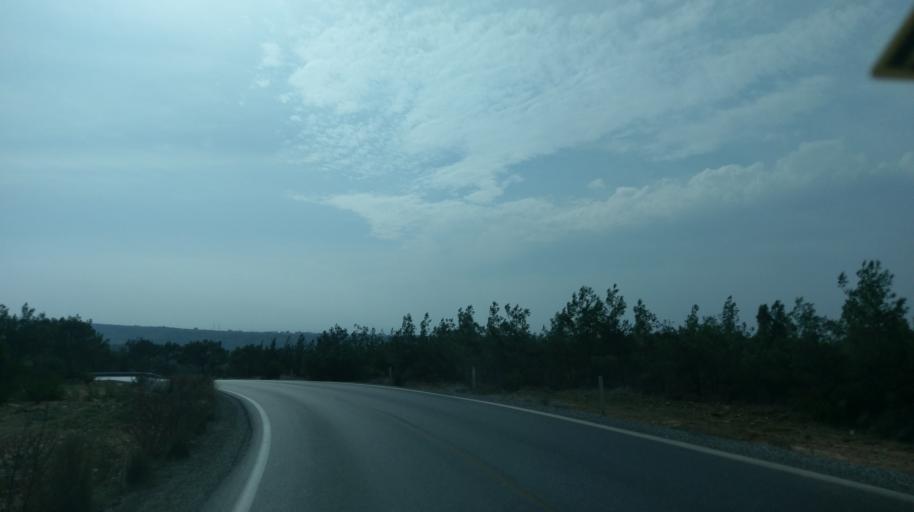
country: CY
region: Lefkosia
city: Morfou
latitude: 35.2710
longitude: 33.0401
